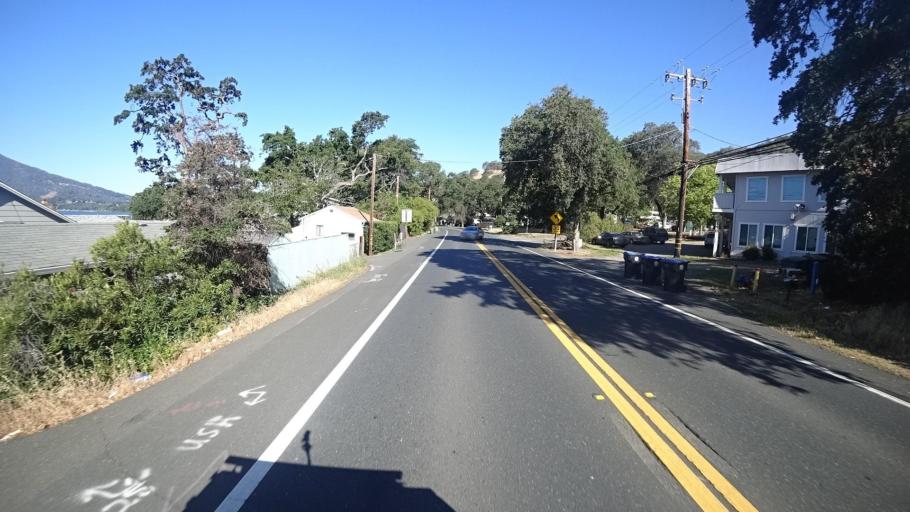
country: US
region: California
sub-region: Lake County
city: Clearlake Oaks
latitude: 39.0240
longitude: -122.7210
